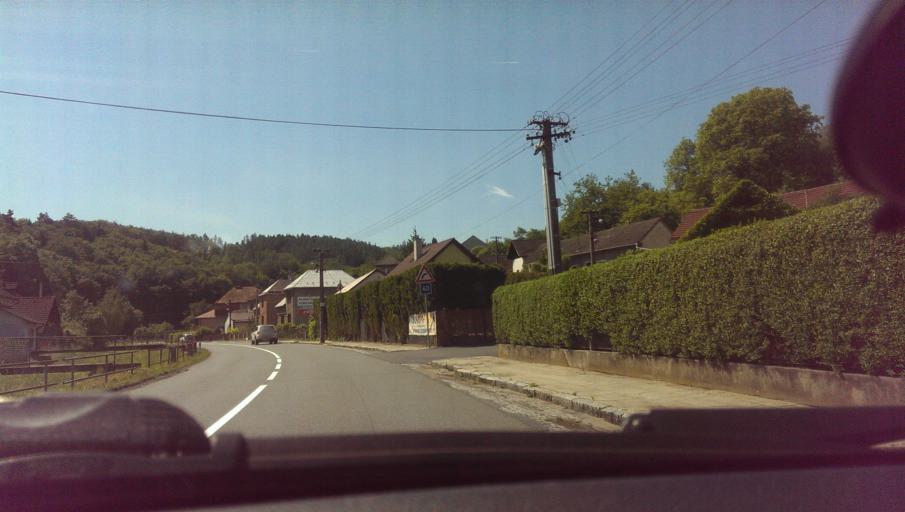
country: CZ
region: Zlin
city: Breznice
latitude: 49.1607
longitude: 17.6344
